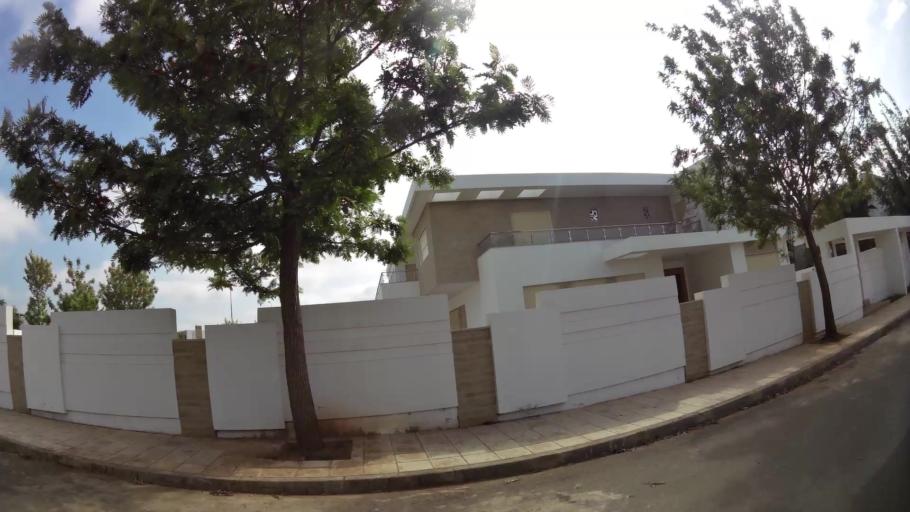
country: MA
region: Rabat-Sale-Zemmour-Zaer
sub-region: Rabat
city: Rabat
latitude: 33.9715
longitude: -6.8482
